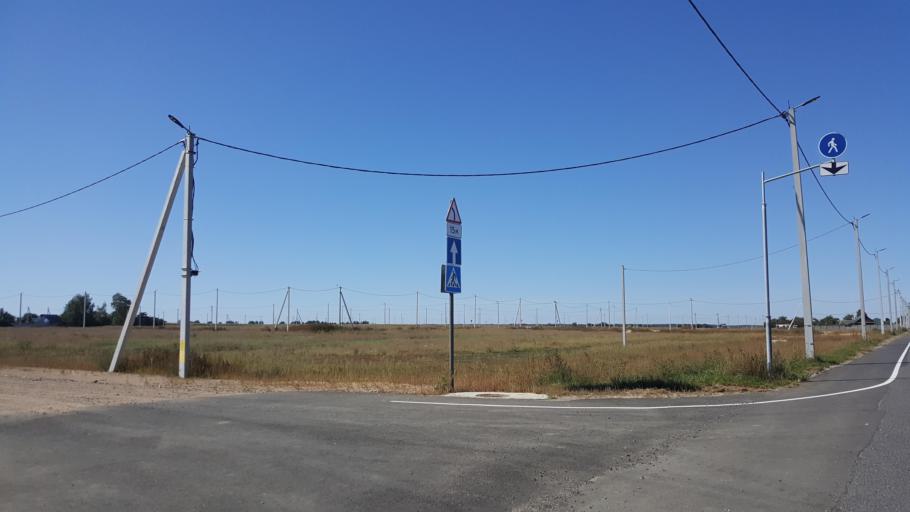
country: BY
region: Brest
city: Charnawchytsy
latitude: 52.2619
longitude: 23.5709
